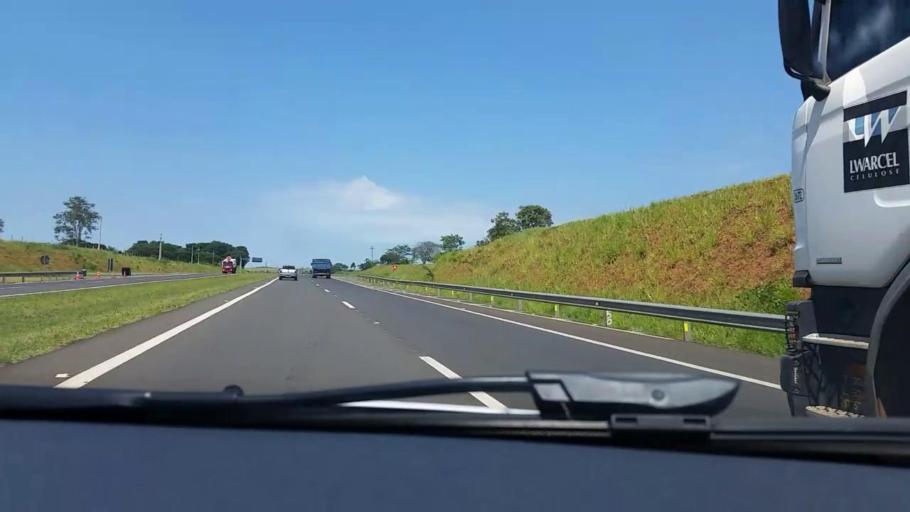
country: BR
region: Sao Paulo
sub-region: Bauru
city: Bauru
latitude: -22.3776
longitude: -49.0609
